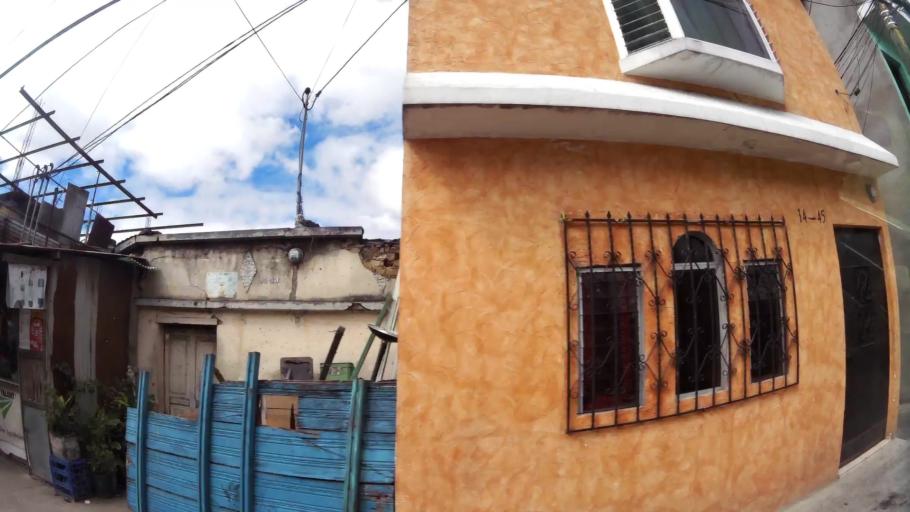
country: GT
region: Guatemala
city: Guatemala City
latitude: 14.6411
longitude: -90.5513
